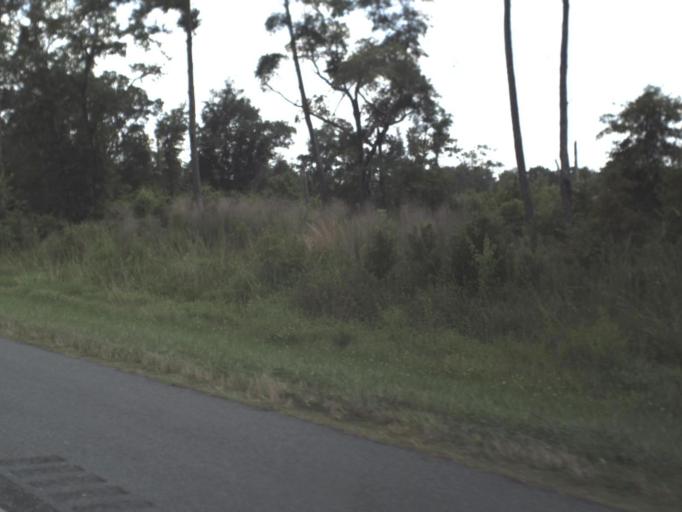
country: US
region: Florida
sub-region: Hamilton County
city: Jasper
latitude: 30.4701
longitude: -82.9685
